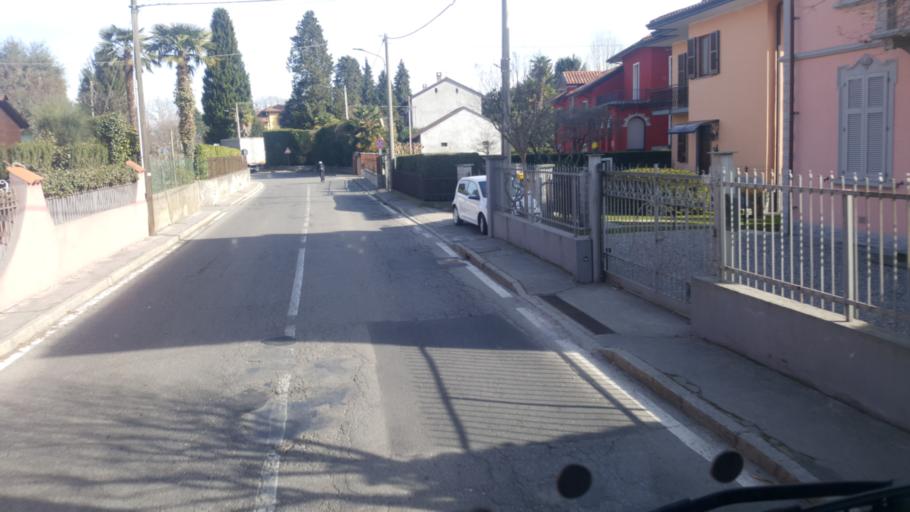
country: IT
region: Lombardy
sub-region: Provincia di Varese
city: Travedona Monate
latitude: 45.8042
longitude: 8.6652
